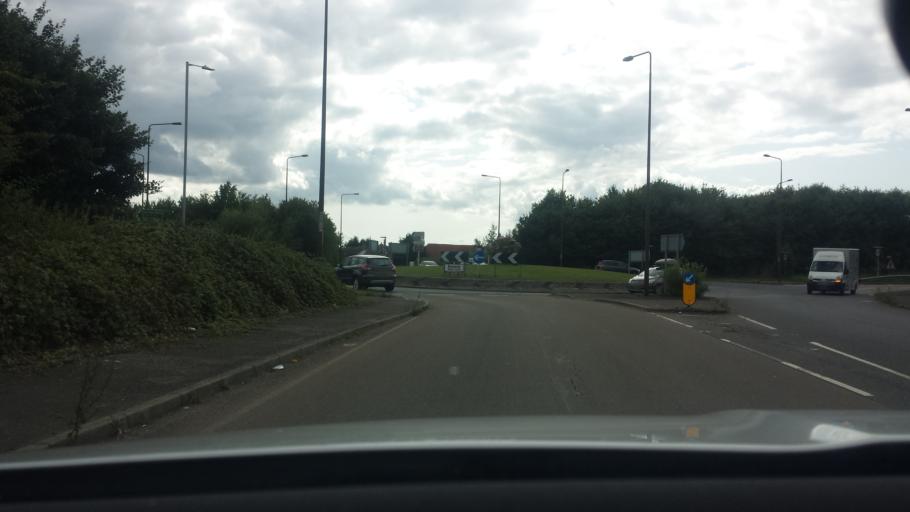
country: GB
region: England
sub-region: Kent
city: East Peckham
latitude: 51.2248
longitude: 0.3976
